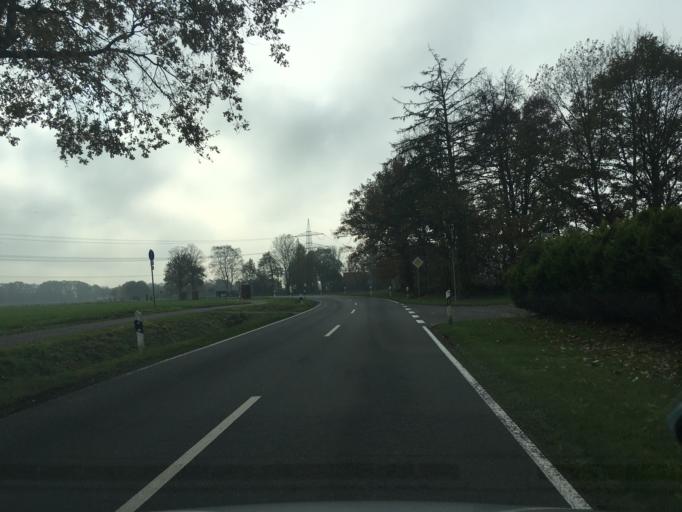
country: DE
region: North Rhine-Westphalia
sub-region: Regierungsbezirk Munster
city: Sudlohn
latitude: 51.9100
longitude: 6.9165
